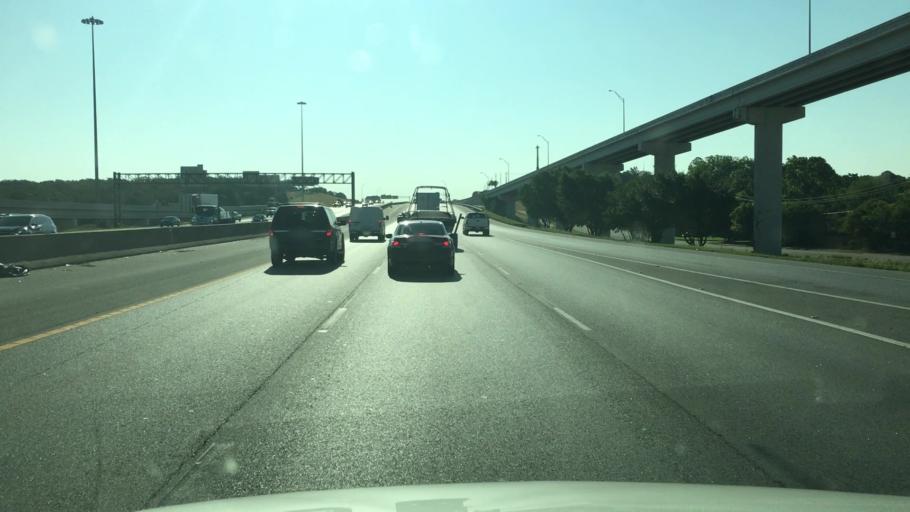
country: US
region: Texas
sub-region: Tarrant County
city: Richland Hills
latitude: 32.7597
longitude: -97.2093
